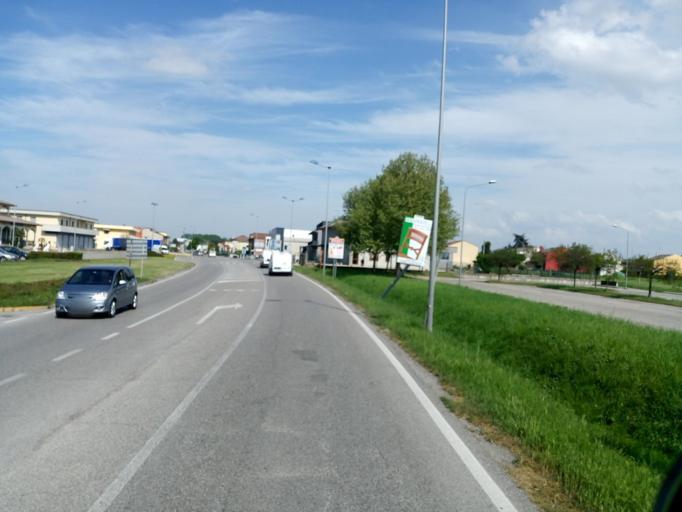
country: IT
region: Veneto
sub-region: Provincia di Verona
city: Casaleone
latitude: 45.1847
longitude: 11.1935
